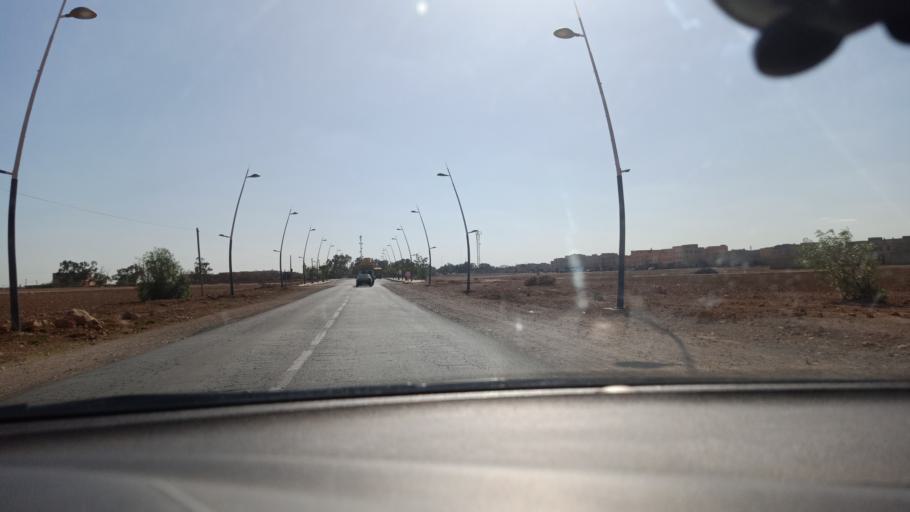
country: MA
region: Doukkala-Abda
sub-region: Safi
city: Youssoufia
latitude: 32.0866
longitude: -8.6190
